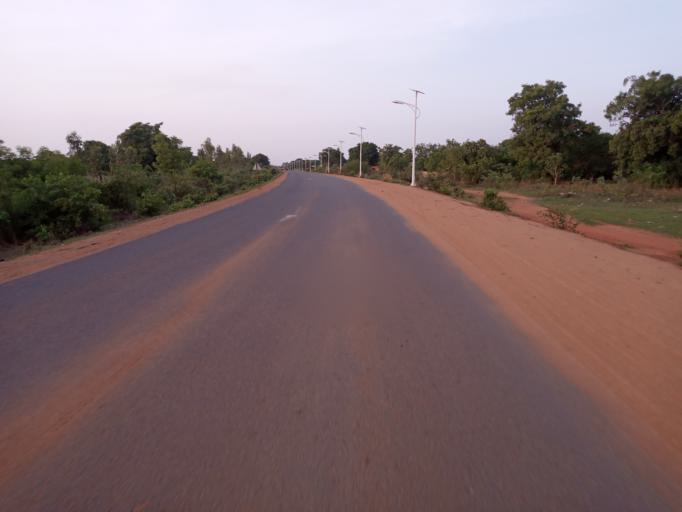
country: ML
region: Bamako
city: Bamako
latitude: 12.2997
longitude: -8.1592
